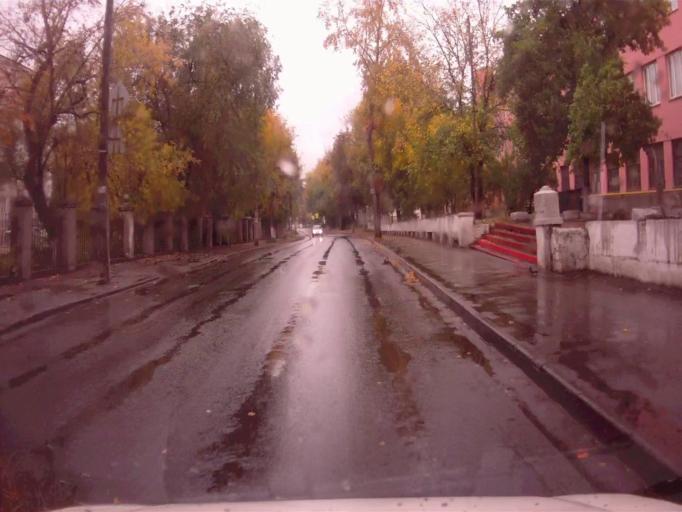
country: RU
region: Chelyabinsk
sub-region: Gorod Chelyabinsk
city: Chelyabinsk
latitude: 55.1916
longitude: 61.4122
